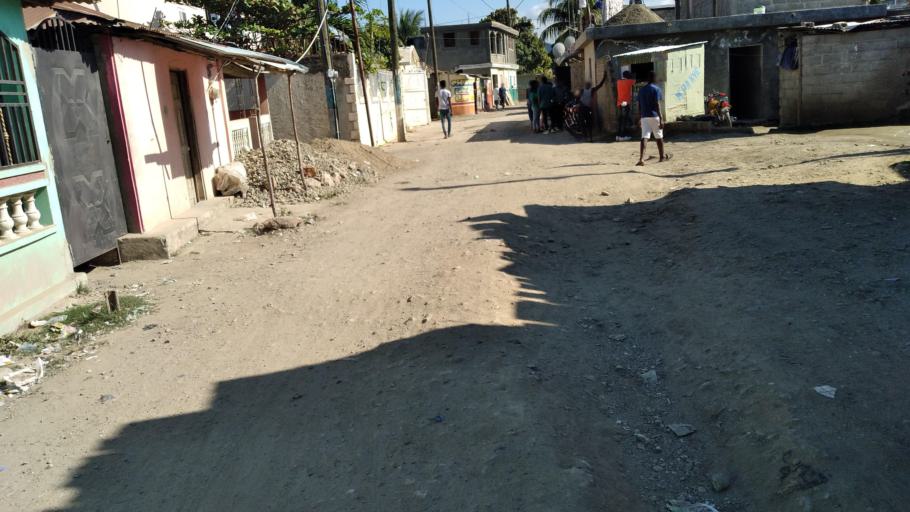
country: HT
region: Nord
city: Limonade
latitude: 19.6709
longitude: -72.1289
